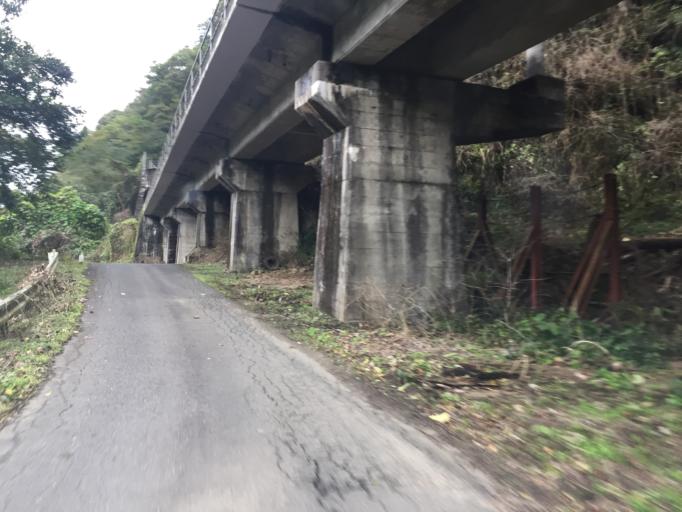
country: JP
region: Miyagi
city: Marumori
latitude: 37.9316
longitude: 140.7213
